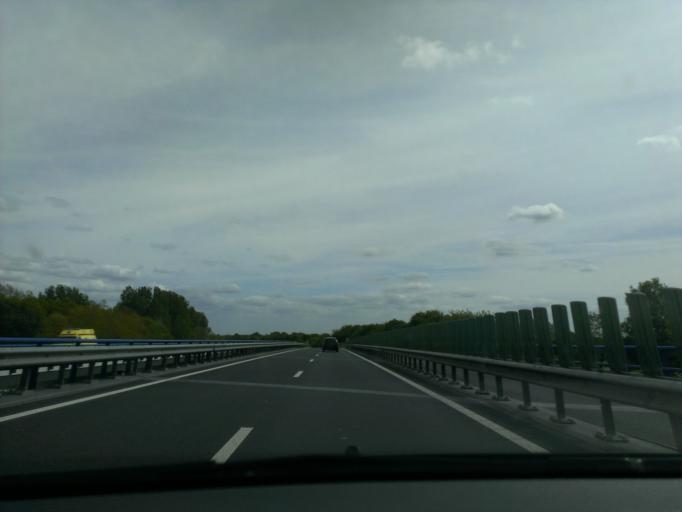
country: NL
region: Gelderland
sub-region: Gemeente Harderwijk
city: Harderwijk
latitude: 52.4114
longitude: 5.5873
